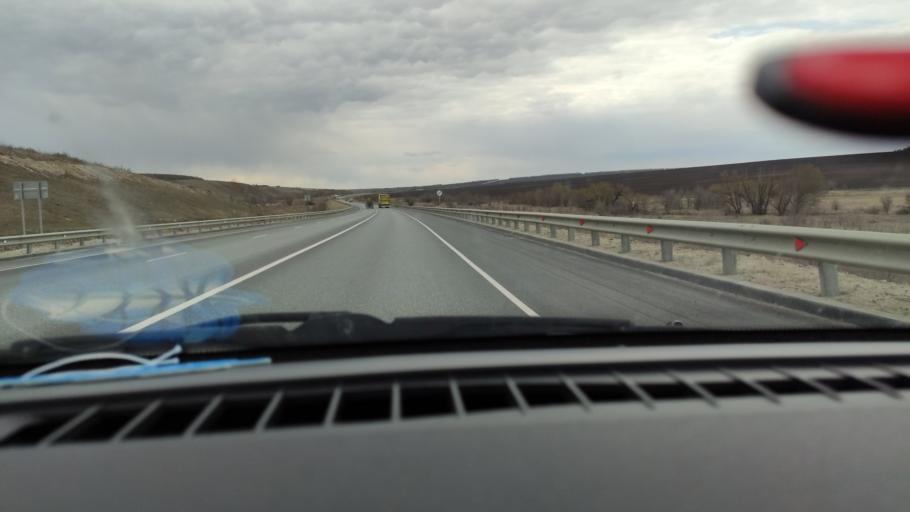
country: RU
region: Saratov
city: Yelshanka
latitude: 51.8690
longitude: 46.5026
